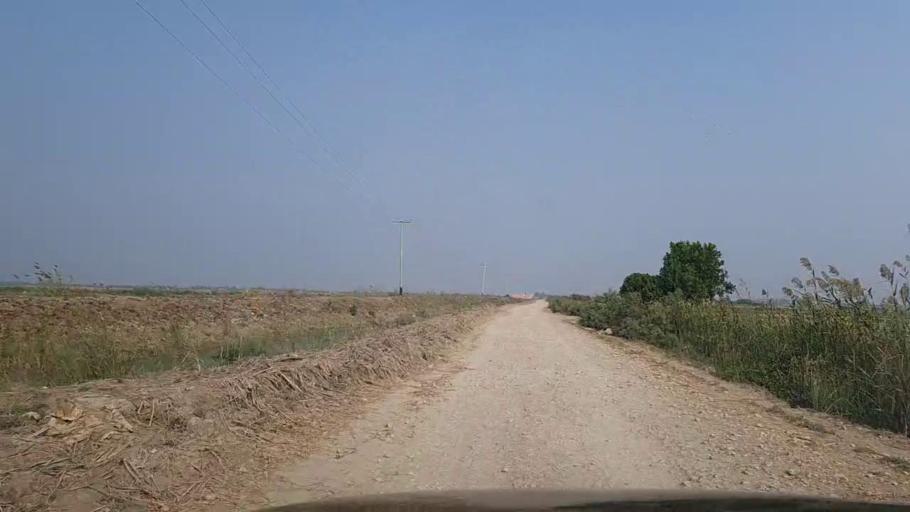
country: PK
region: Sindh
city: Thatta
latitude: 24.7535
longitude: 67.8722
